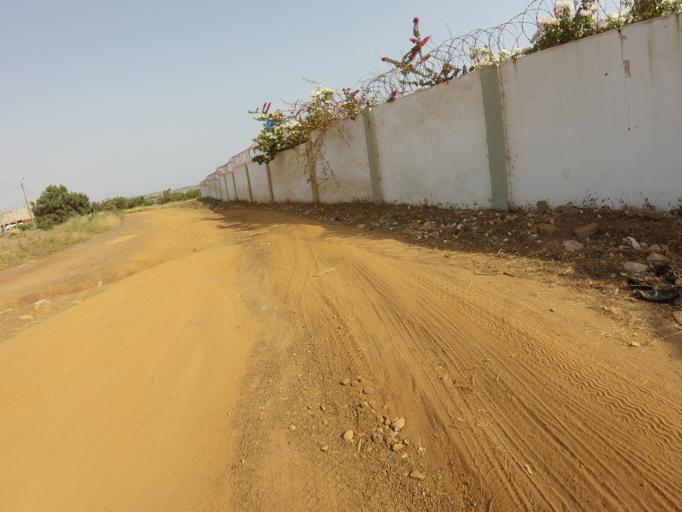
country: GH
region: Greater Accra
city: Tema
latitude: 5.7048
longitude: 0.0598
